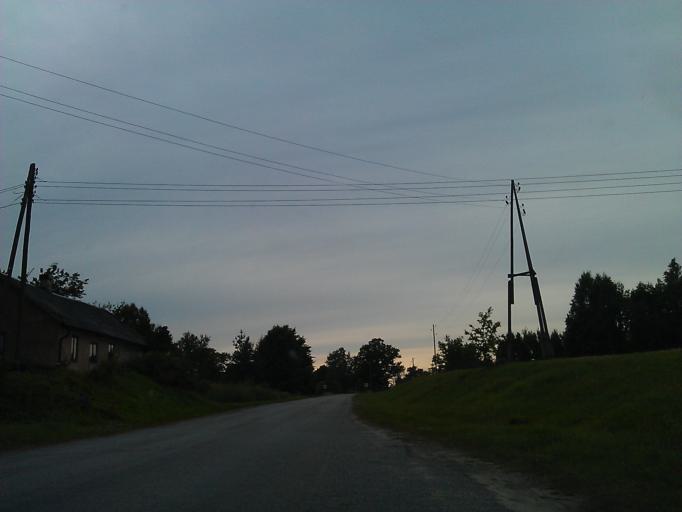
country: LV
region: Ligatne
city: Ligatne
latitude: 57.1873
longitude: 25.0517
